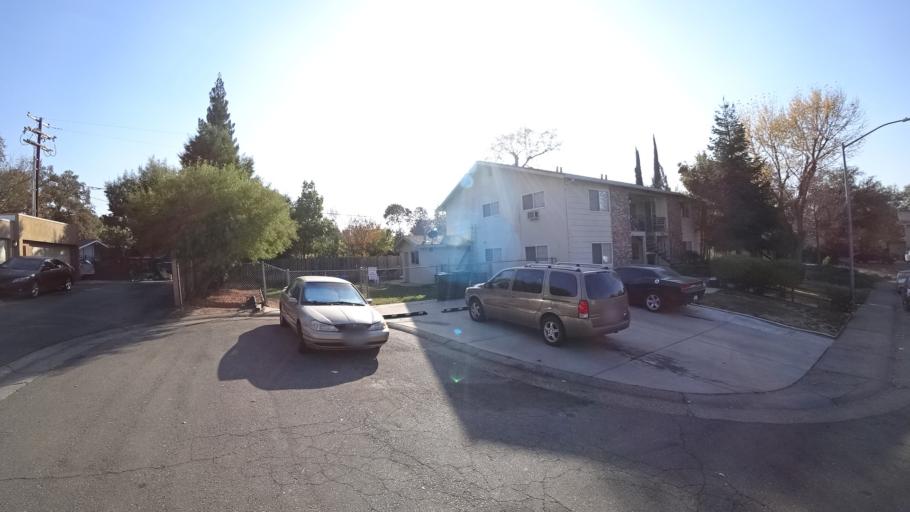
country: US
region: California
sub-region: Sacramento County
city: Citrus Heights
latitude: 38.7010
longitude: -121.2730
